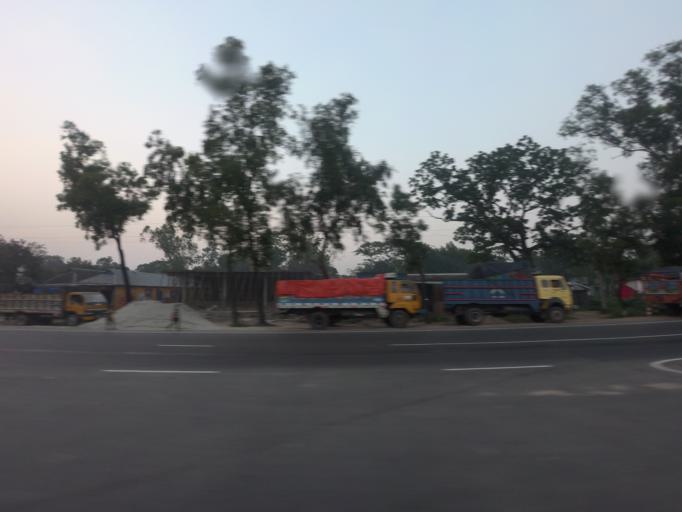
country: BD
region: Chittagong
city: Comilla
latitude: 23.4820
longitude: 91.0531
